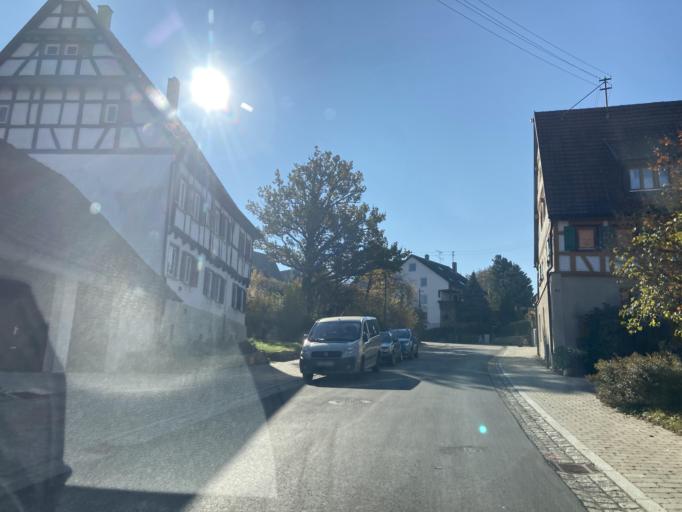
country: DE
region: Baden-Wuerttemberg
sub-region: Tuebingen Region
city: Nehren
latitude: 48.4351
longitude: 9.0658
